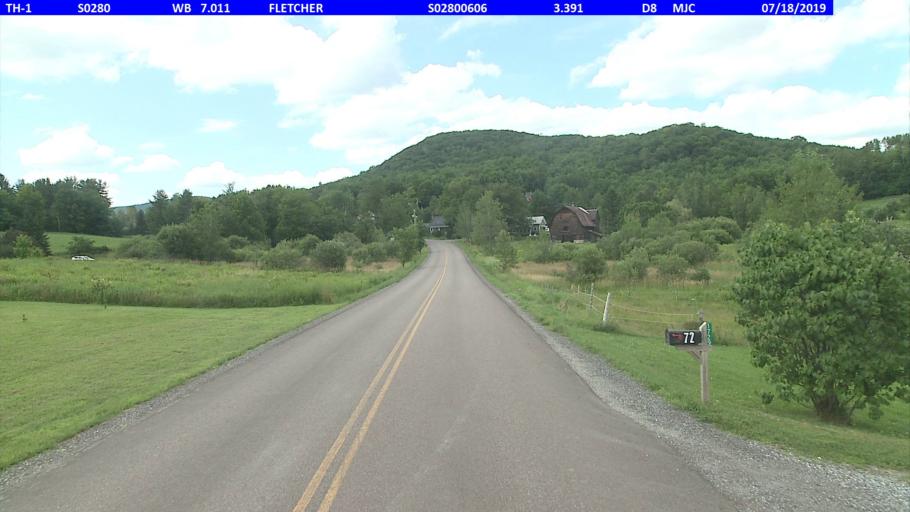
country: US
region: Vermont
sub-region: Lamoille County
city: Johnson
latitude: 44.6823
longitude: -72.8839
